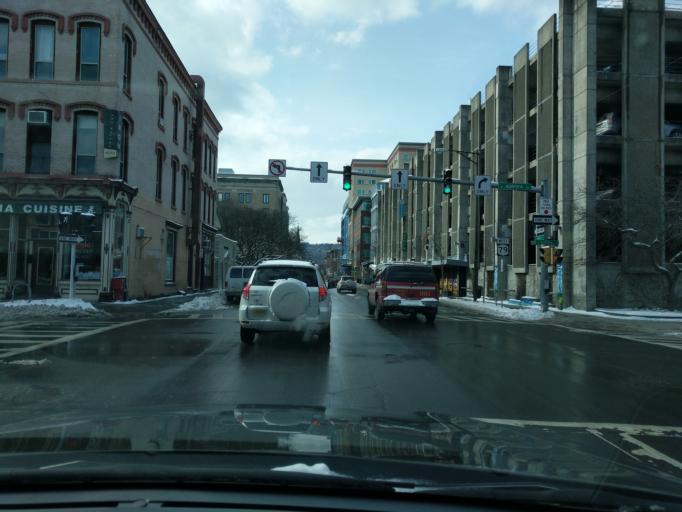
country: US
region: New York
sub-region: Tompkins County
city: Ithaca
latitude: 42.4405
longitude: -76.4955
